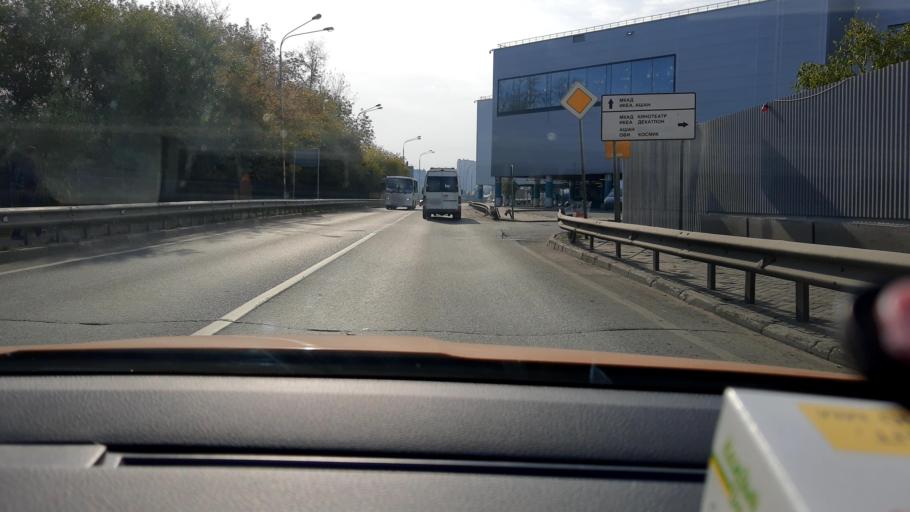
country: RU
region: Moskovskaya
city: Kotel'niki
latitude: 55.6590
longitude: 37.8479
